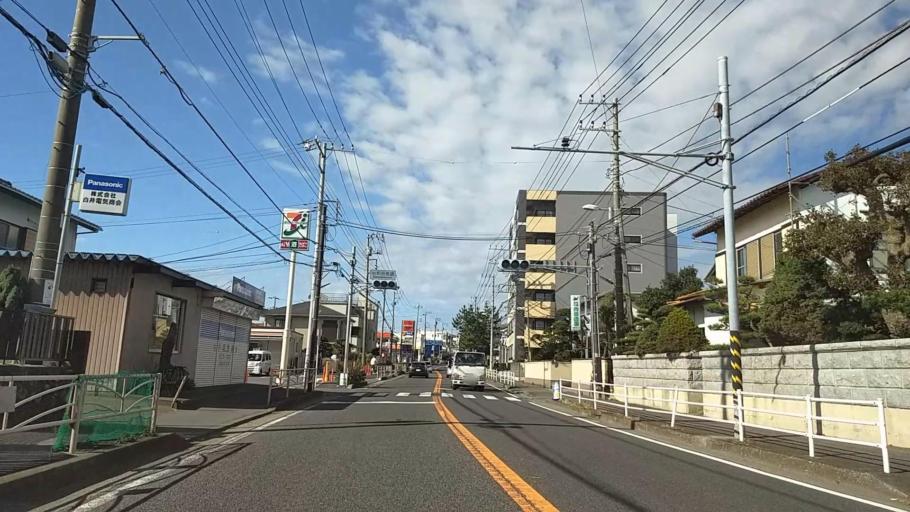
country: JP
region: Kanagawa
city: Chigasaki
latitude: 35.3370
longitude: 139.4288
